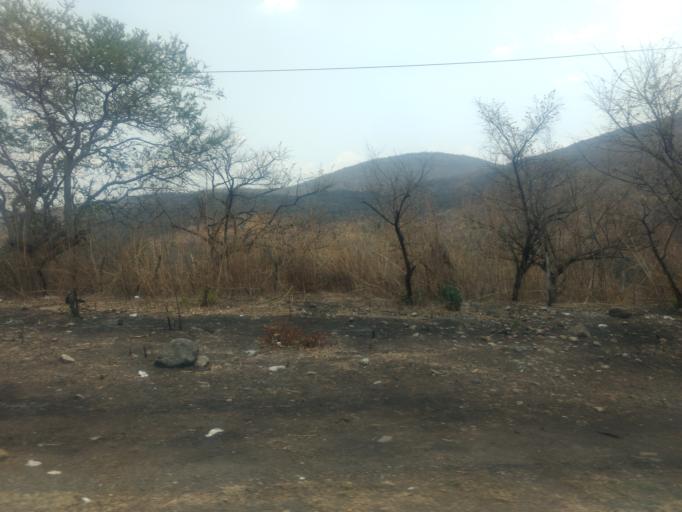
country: MX
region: Morelos
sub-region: Mazatepec
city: Cuauchichinola
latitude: 18.6555
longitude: -99.4092
